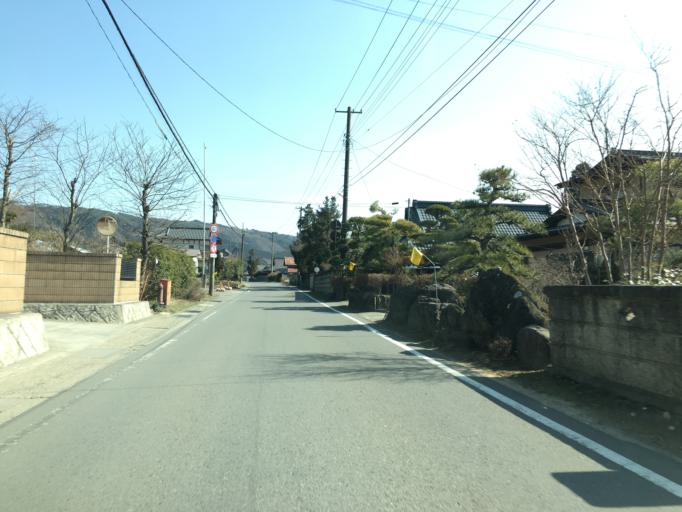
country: JP
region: Ibaraki
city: Daigo
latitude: 36.8399
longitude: 140.4397
